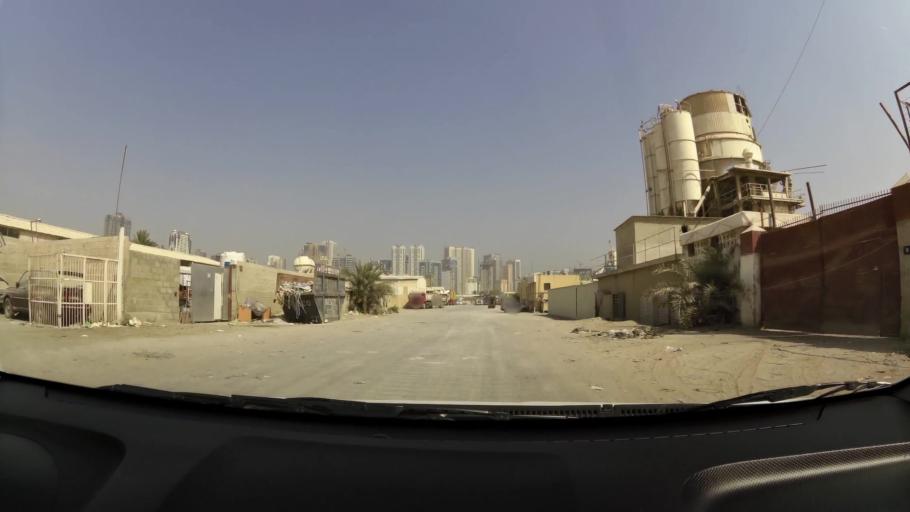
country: AE
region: Ash Shariqah
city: Sharjah
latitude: 25.3090
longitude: 55.3870
